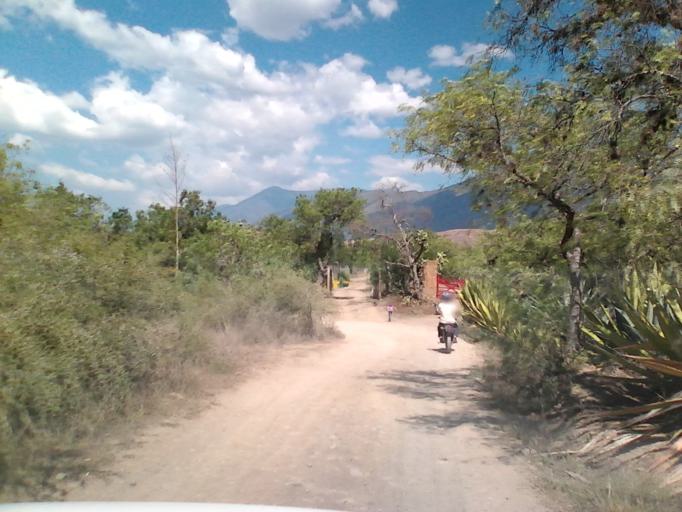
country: CO
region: Boyaca
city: Sachica
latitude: 5.6057
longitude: -73.5572
